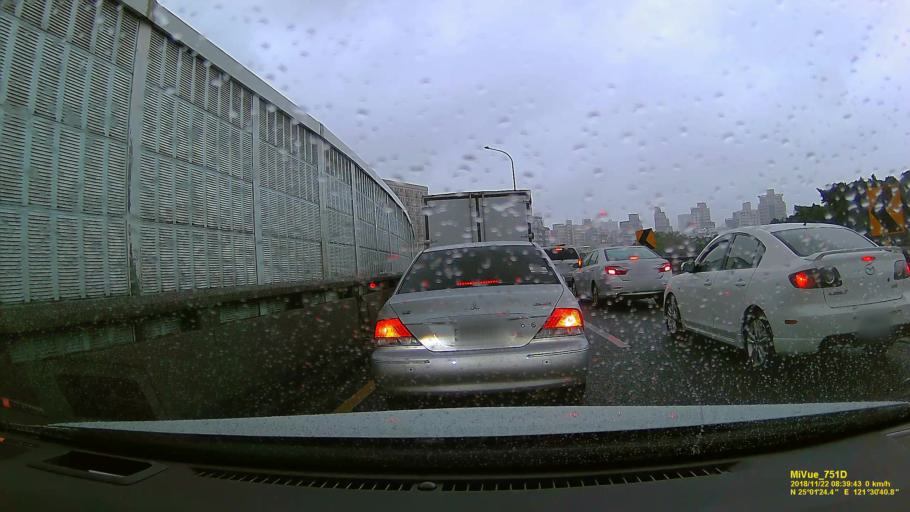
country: TW
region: Taipei
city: Taipei
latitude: 25.0236
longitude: 121.5117
